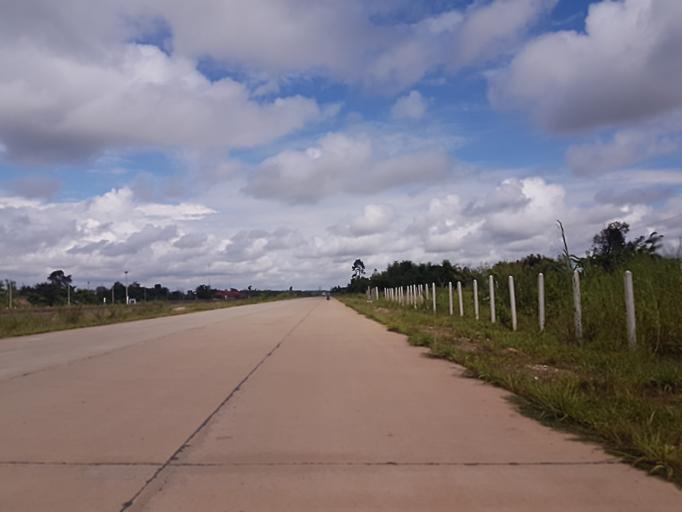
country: TH
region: Nong Khai
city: Nong Khai
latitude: 17.8993
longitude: 102.7117
